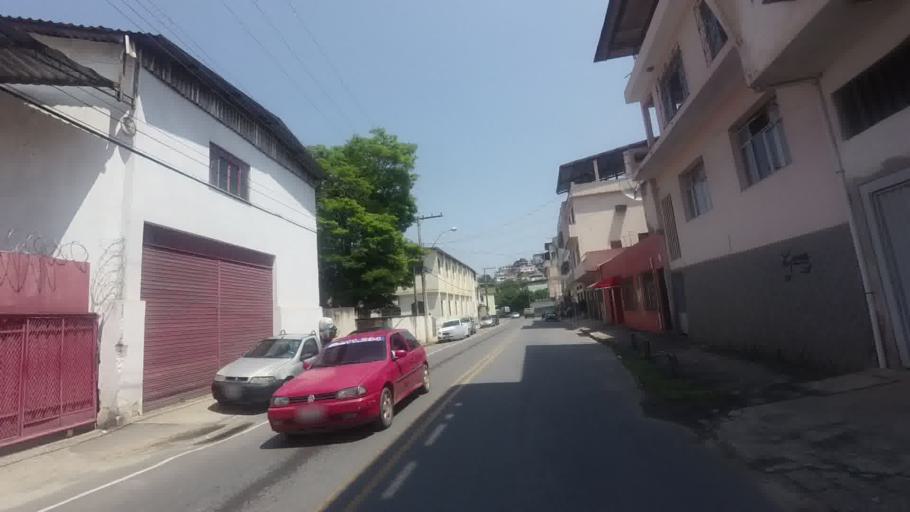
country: BR
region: Espirito Santo
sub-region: Cachoeiro De Itapemirim
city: Cachoeiro de Itapemirim
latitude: -20.8527
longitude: -41.0957
